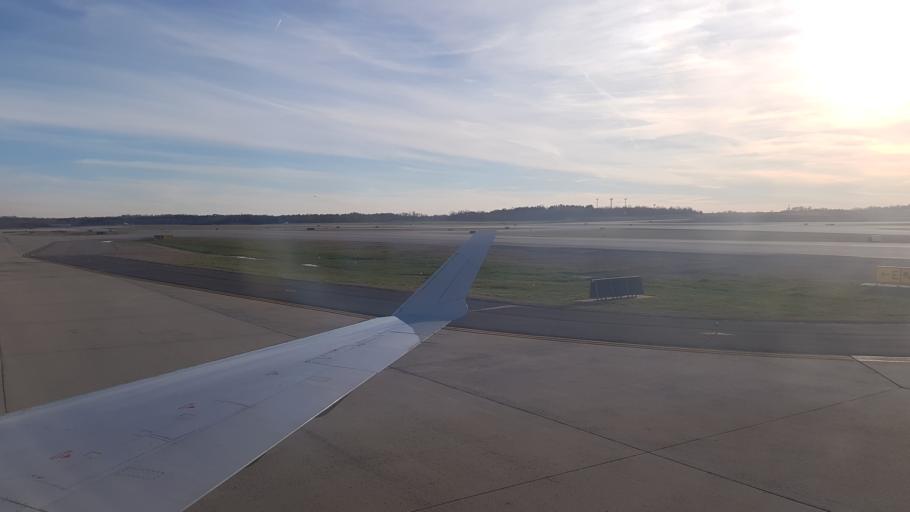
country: US
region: North Carolina
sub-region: Gaston County
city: Belmont
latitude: 35.2159
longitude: -80.9495
